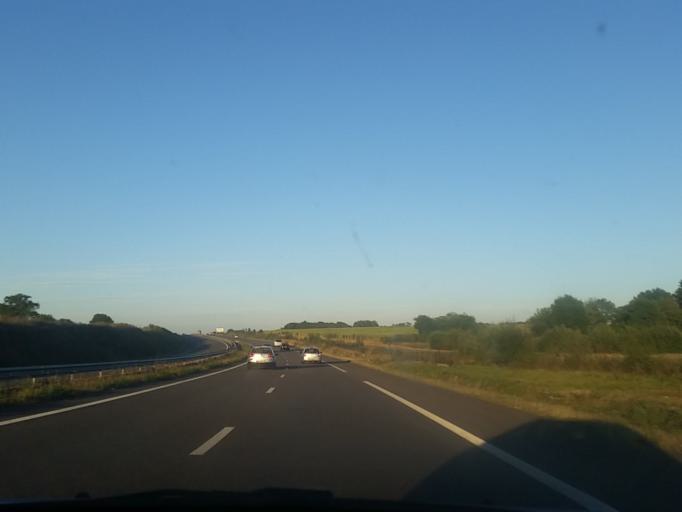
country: FR
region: Pays de la Loire
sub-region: Departement de la Loire-Atlantique
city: Le Pellerin
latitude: 47.1837
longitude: -1.7647
